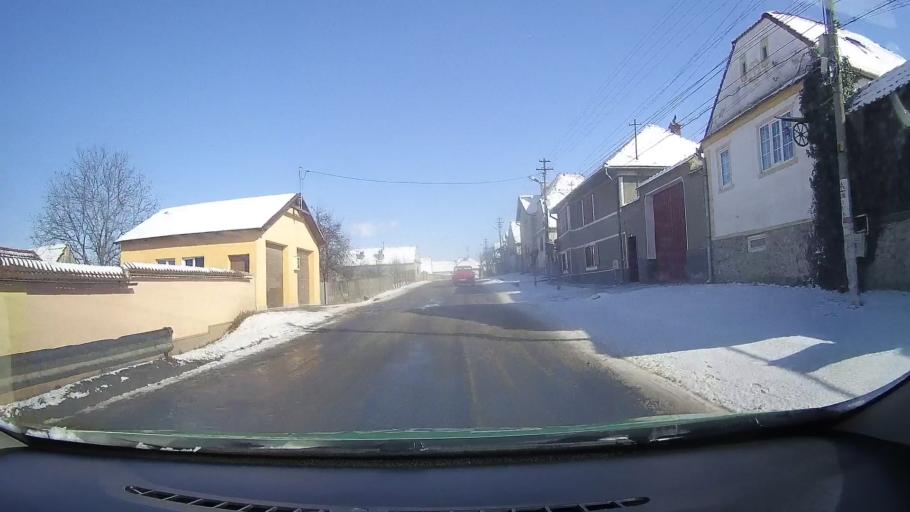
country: RO
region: Sibiu
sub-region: Comuna Avrig
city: Avrig
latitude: 45.7226
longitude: 24.3717
